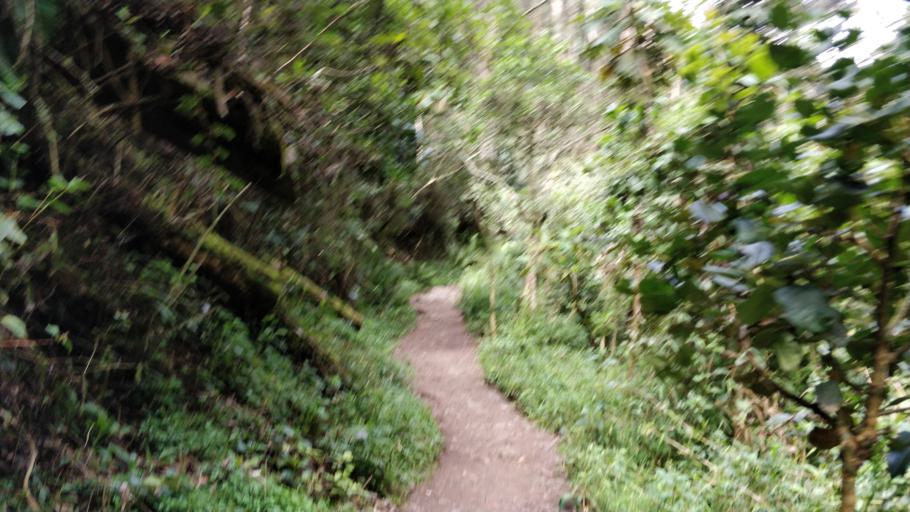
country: CO
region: Bogota D.C.
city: Barrio San Luis
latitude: 4.6445
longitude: -74.0432
